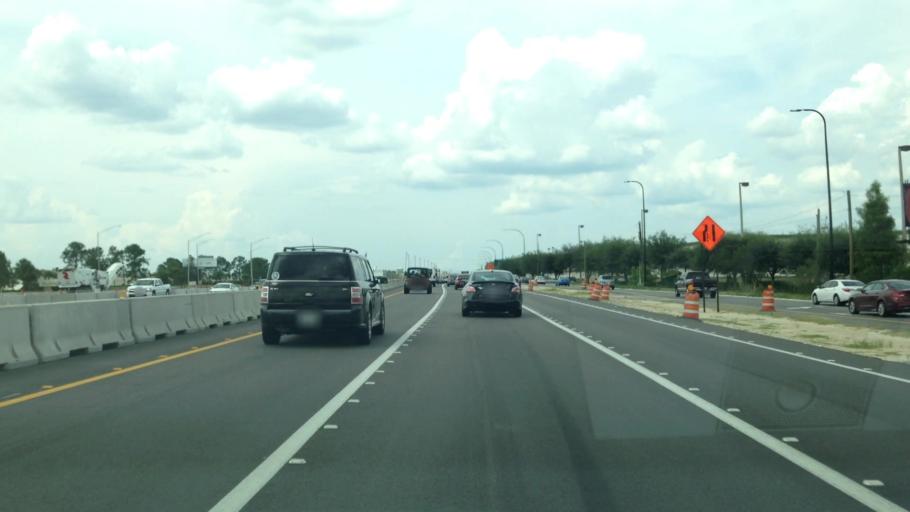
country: US
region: Florida
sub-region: Orange County
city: Oak Ridge
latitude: 28.4946
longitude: -81.4318
